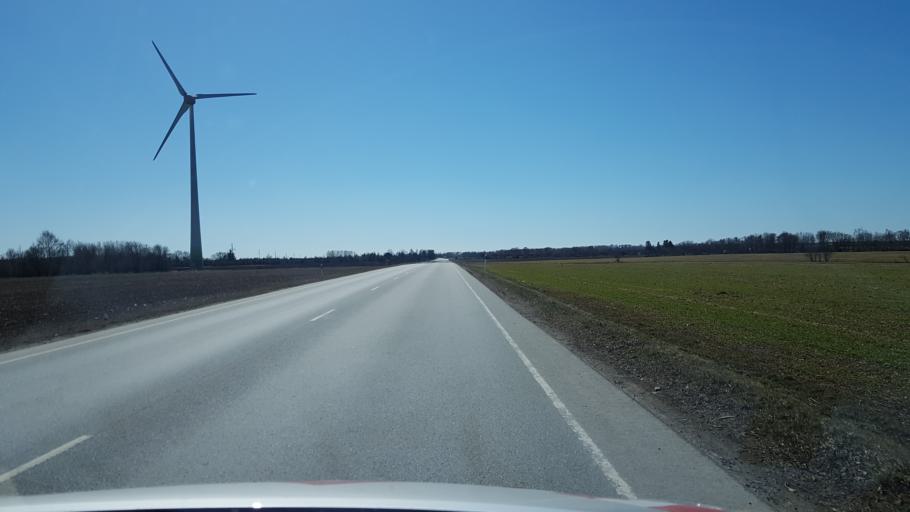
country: EE
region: Laeaene-Virumaa
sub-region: Viru-Nigula vald
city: Kunda
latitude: 59.4894
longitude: 26.4994
